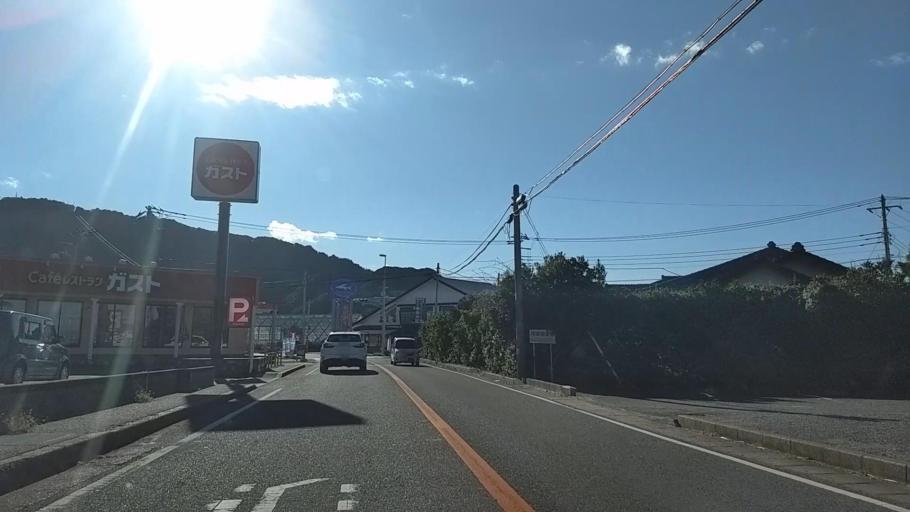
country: JP
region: Chiba
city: Futtsu
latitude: 35.1690
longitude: 139.8193
